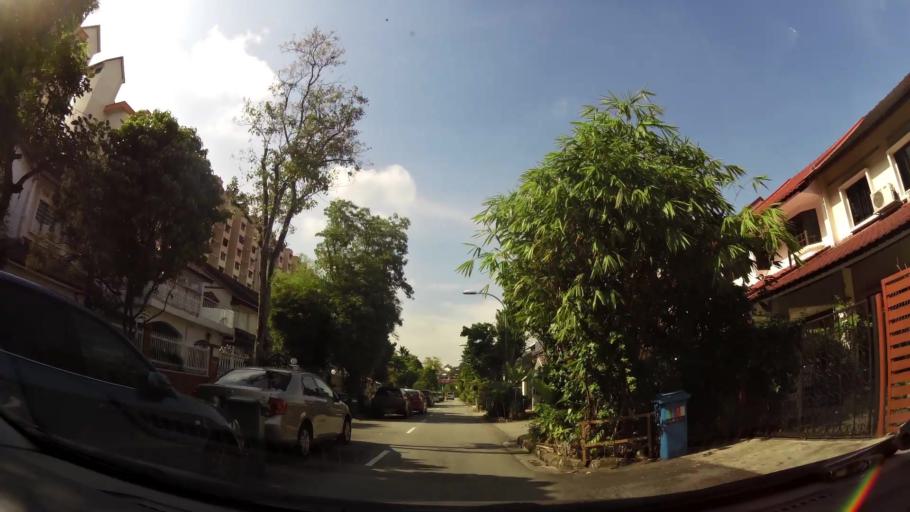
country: SG
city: Singapore
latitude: 1.3552
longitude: 103.8359
